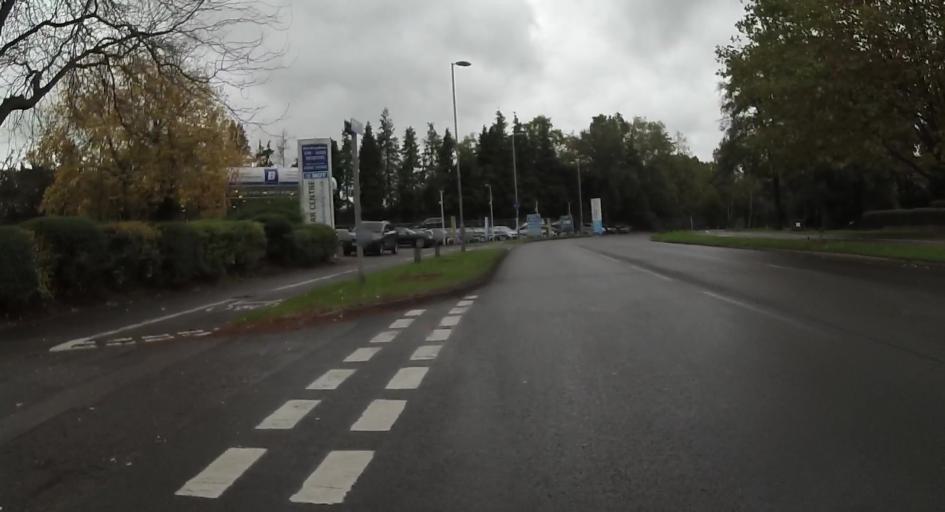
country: GB
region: England
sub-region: Surrey
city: Woking
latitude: 51.3280
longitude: -0.5359
